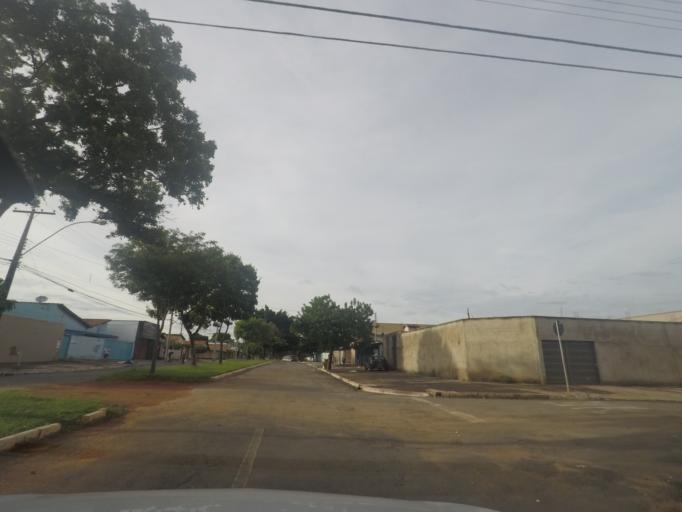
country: BR
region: Goias
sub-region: Goiania
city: Goiania
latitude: -16.6855
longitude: -49.3513
